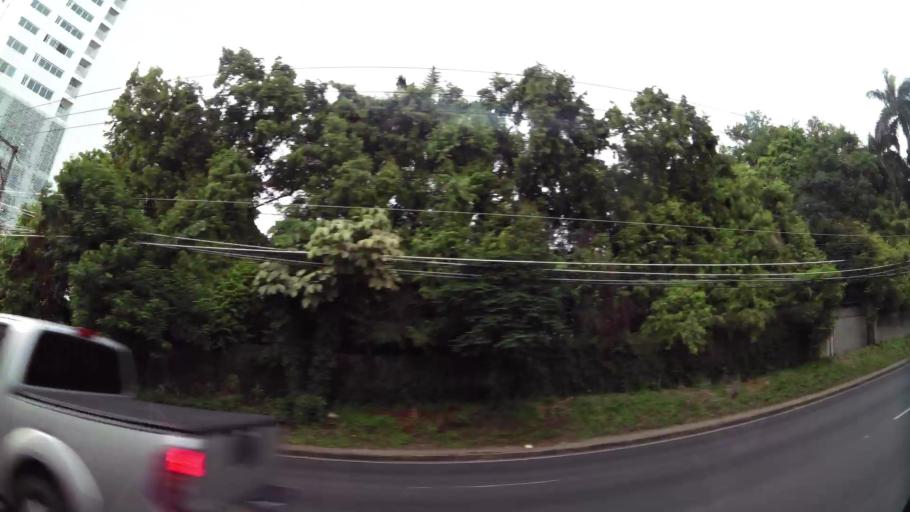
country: PA
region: Panama
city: Panama
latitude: 8.9972
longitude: -79.5054
